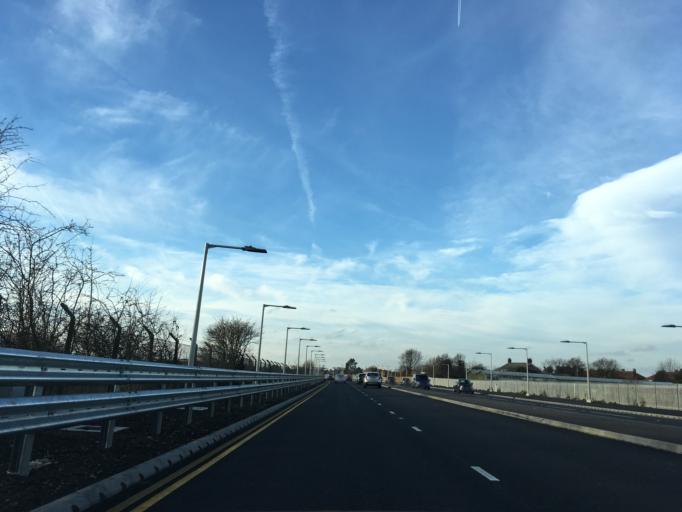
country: GB
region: England
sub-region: Manchester
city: Ringway
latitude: 53.3634
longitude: -2.2480
